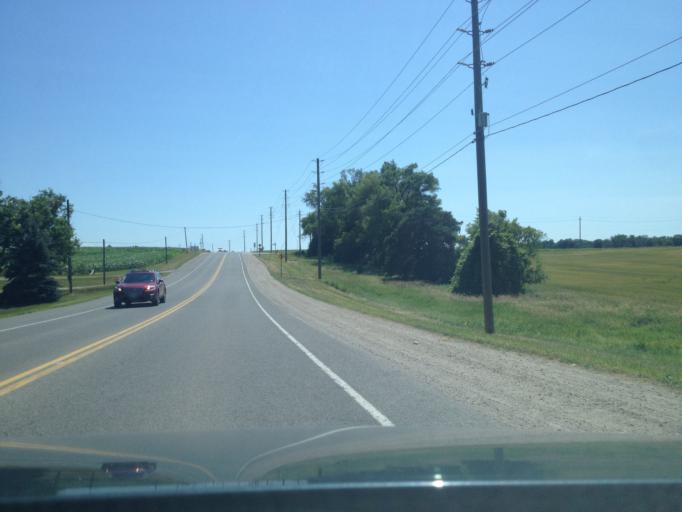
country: CA
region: Ontario
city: Waterloo
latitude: 43.5361
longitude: -80.5117
